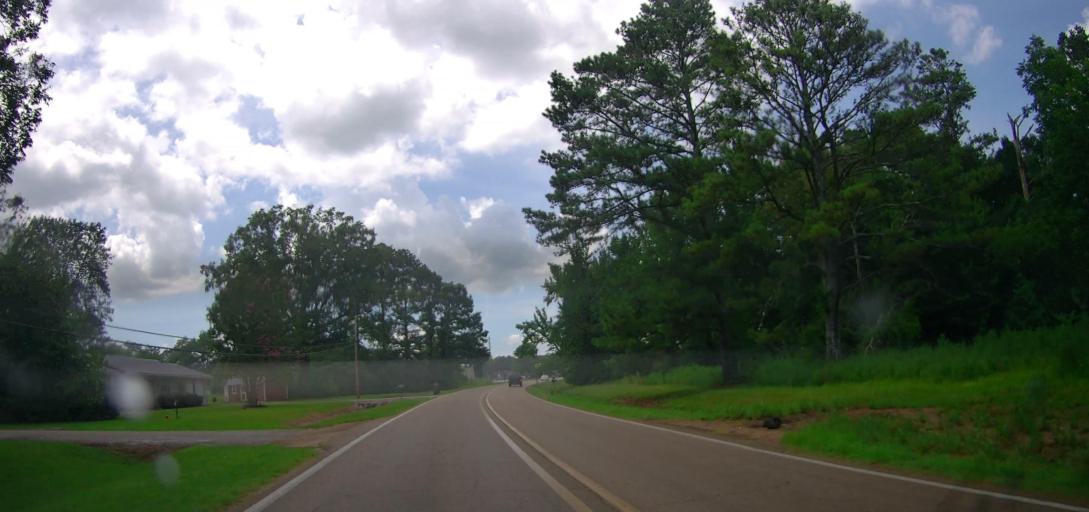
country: US
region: Mississippi
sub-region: Lee County
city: Shannon
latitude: 34.1233
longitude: -88.7167
